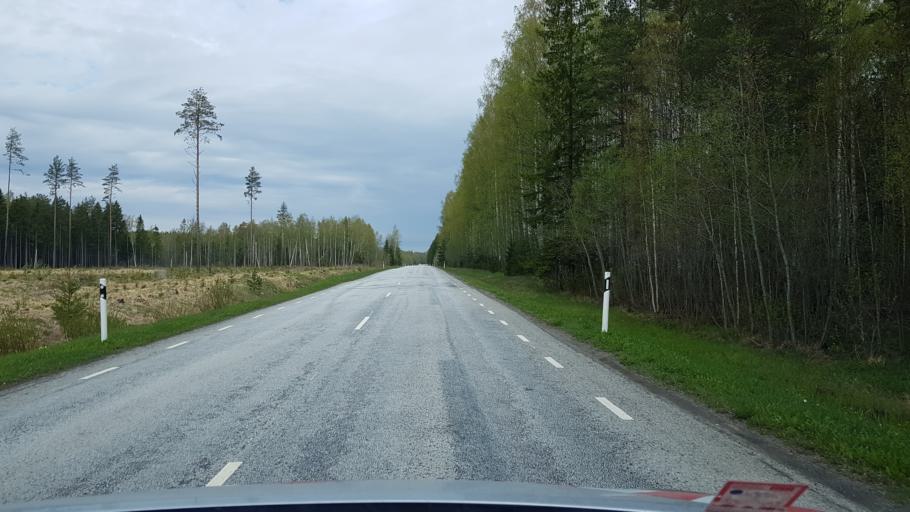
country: EE
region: Ida-Virumaa
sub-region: Toila vald
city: Toila
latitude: 59.3821
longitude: 27.5066
